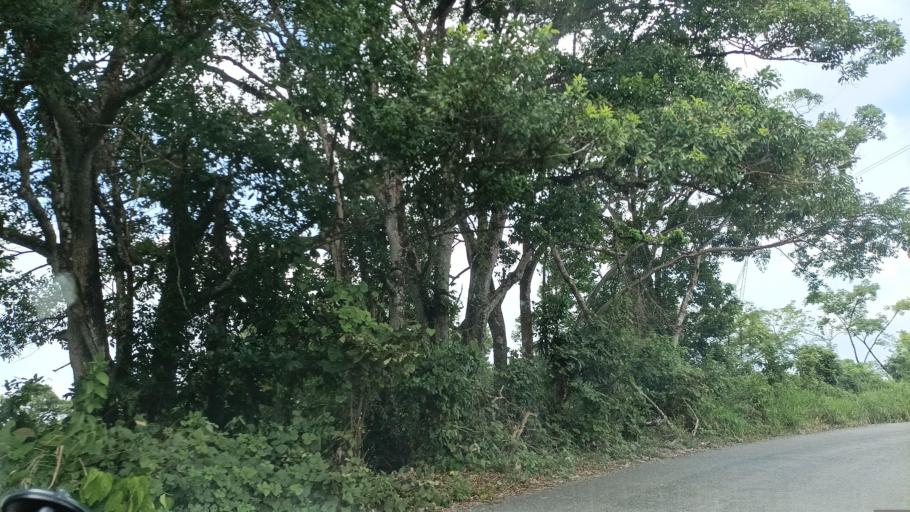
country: MX
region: Veracruz
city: Las Choapas
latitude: 17.7872
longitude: -94.1103
